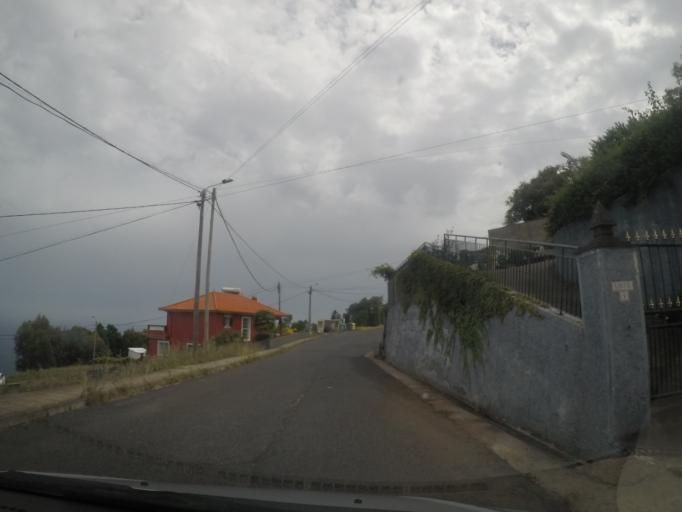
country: PT
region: Madeira
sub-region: Santa Cruz
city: Santa Cruz
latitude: 32.6776
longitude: -16.8093
